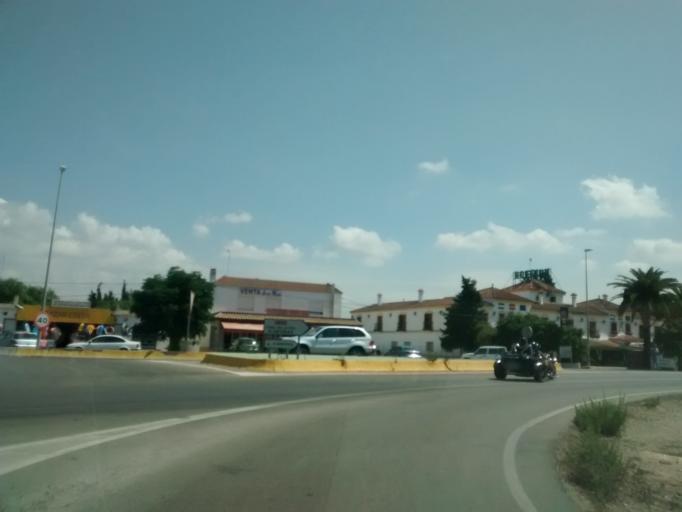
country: ES
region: Andalusia
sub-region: Provincia de Cadiz
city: Conil de la Frontera
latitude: 36.3380
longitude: -6.0936
